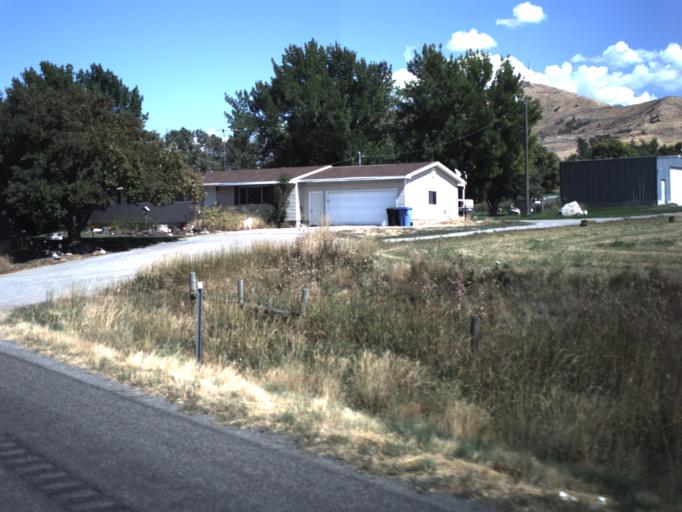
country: US
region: Utah
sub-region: Cache County
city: Smithfield
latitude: 41.8628
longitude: -111.8299
